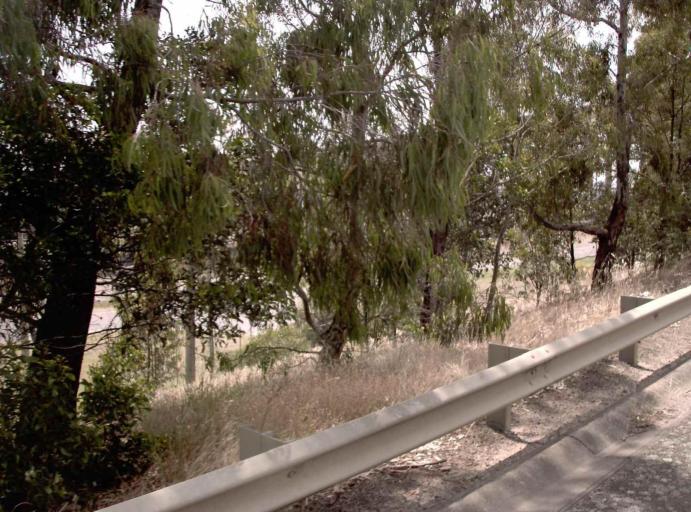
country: AU
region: Victoria
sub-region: Latrobe
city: Traralgon
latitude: -38.2497
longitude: 146.5740
